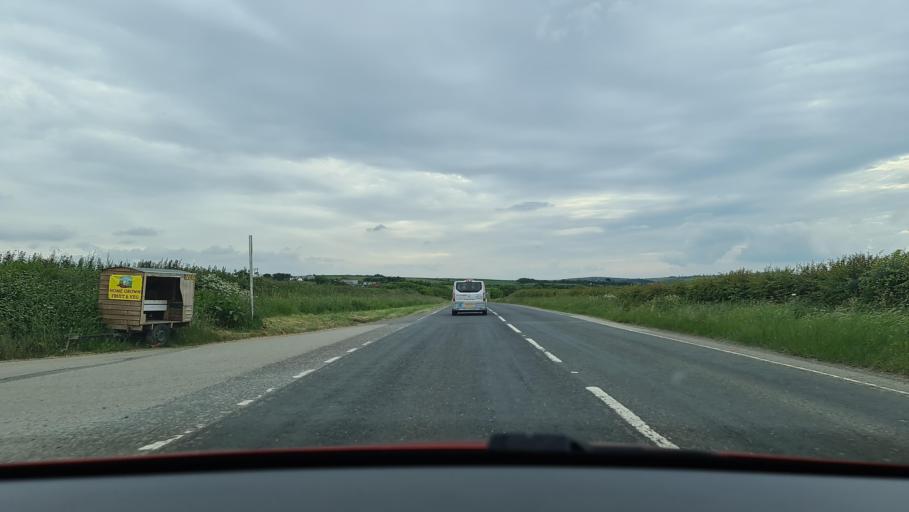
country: GB
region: England
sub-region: Cornwall
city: Poundstock
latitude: 50.7824
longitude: -4.5368
